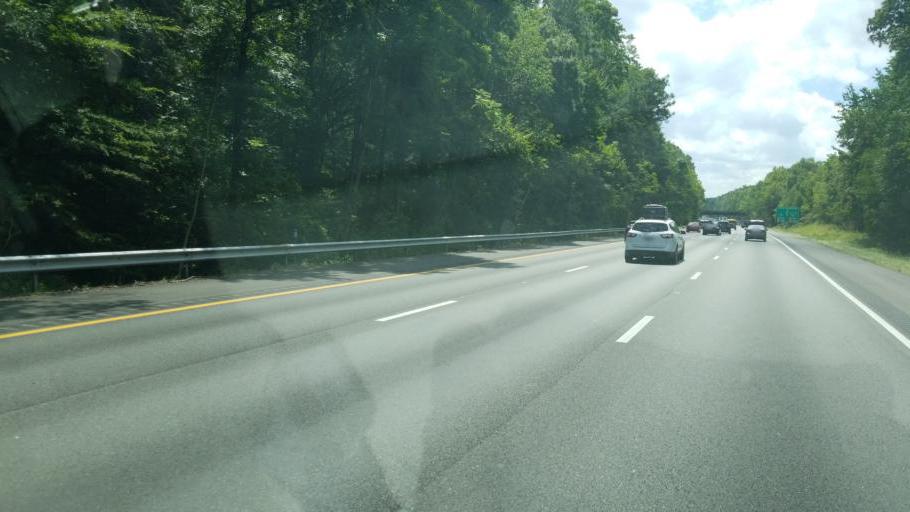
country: US
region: Virginia
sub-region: Hanover County
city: Ashland
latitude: 37.8032
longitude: -77.4612
